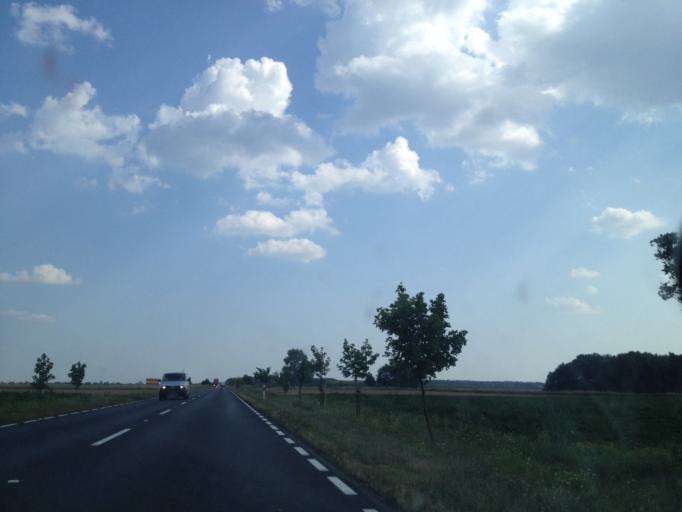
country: PL
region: Greater Poland Voivodeship
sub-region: Powiat poznanski
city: Kornik
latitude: 52.2377
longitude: 17.0587
